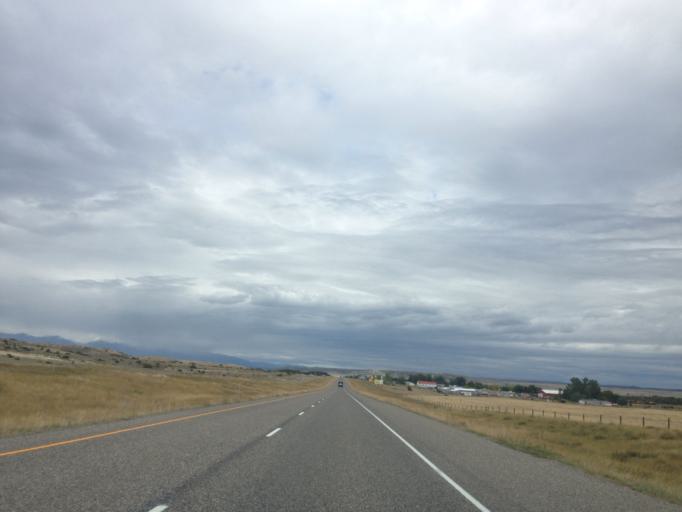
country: US
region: Montana
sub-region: Sweet Grass County
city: Big Timber
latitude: 45.7553
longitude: -109.7812
